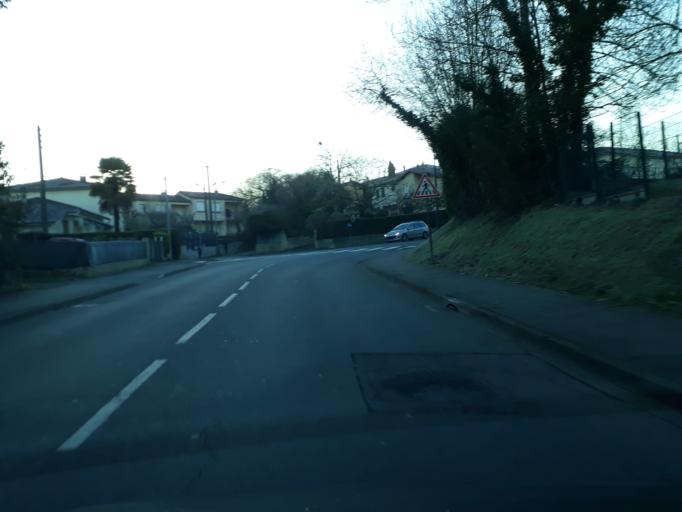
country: FR
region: Midi-Pyrenees
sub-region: Departement du Gers
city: Auch
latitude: 43.6375
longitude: 0.5959
